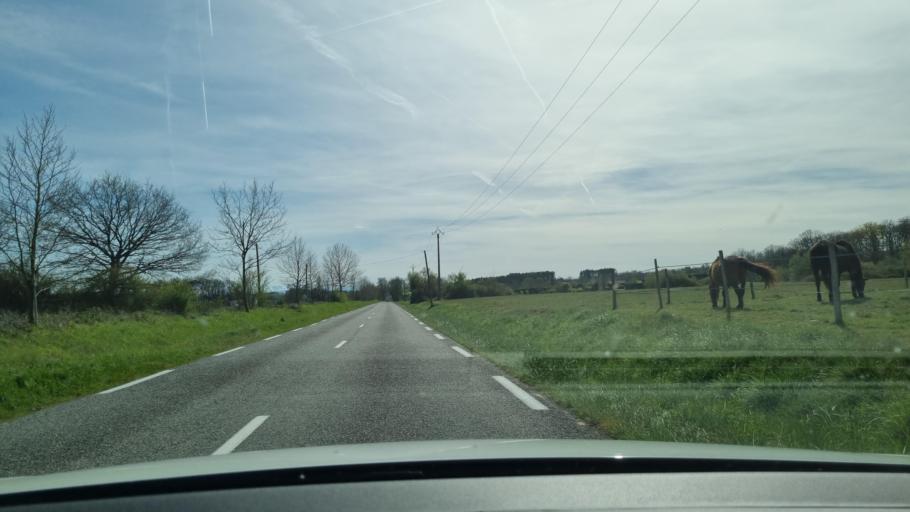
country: FR
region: Midi-Pyrenees
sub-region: Departement du Gers
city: Lombez
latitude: 43.4099
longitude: 0.8027
